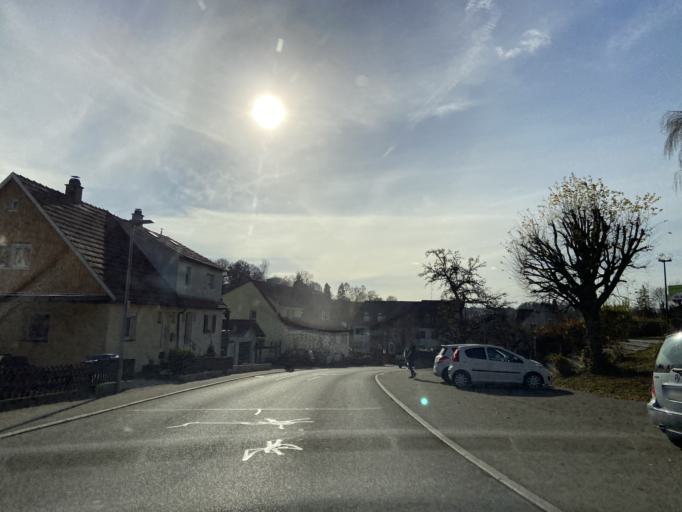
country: DE
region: Baden-Wuerttemberg
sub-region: Tuebingen Region
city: Sigmaringen
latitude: 48.0929
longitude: 9.2302
